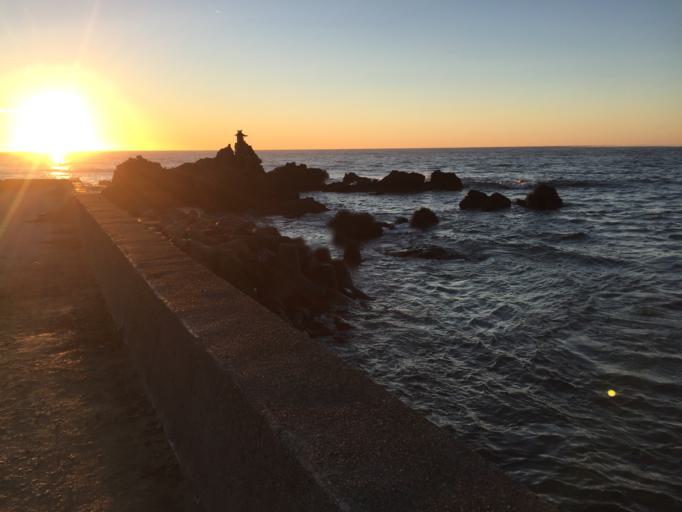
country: JP
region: Ibaraki
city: Kitaibaraki
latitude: 36.7943
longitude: 140.7570
